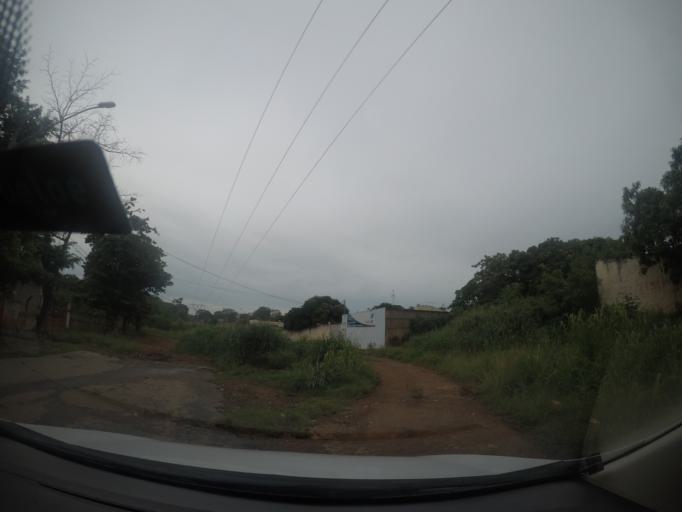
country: BR
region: Goias
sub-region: Goiania
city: Goiania
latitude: -16.6363
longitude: -49.2435
